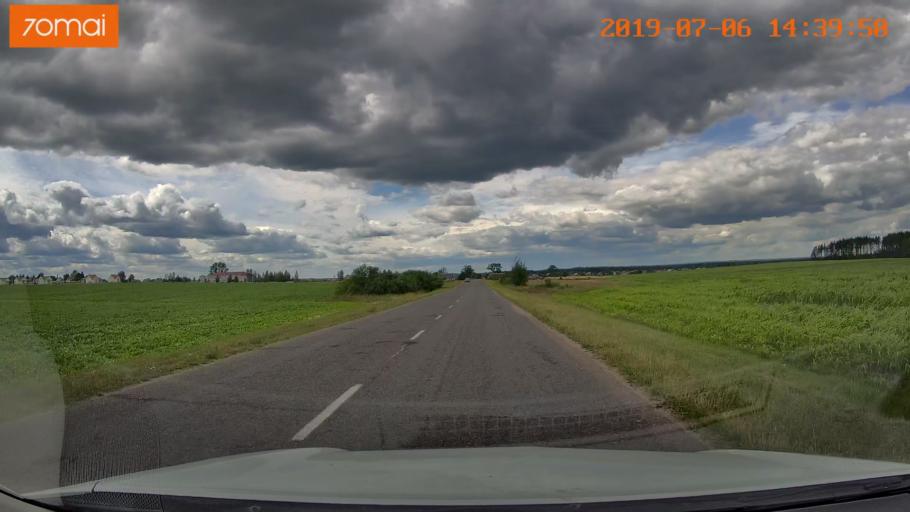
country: BY
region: Minsk
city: Ivyanyets
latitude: 53.9196
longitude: 26.6828
